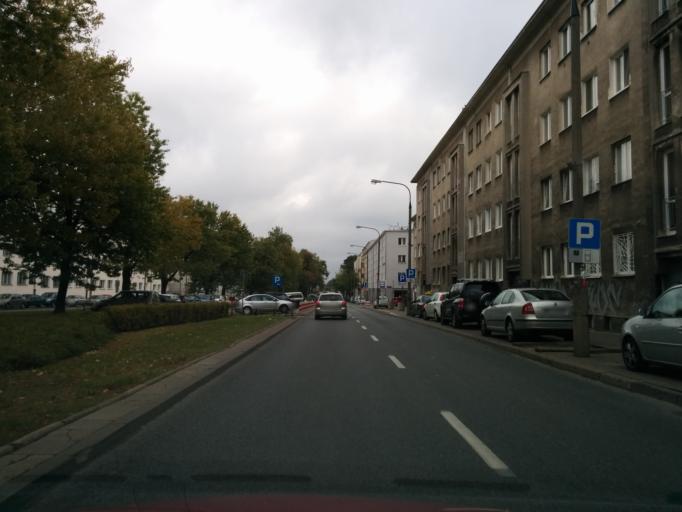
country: PL
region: Masovian Voivodeship
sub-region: Warszawa
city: Zoliborz
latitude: 52.2668
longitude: 20.9790
